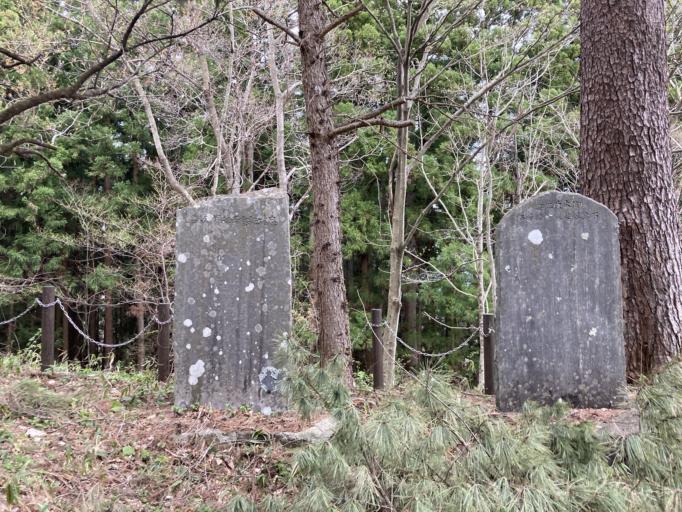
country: JP
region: Iwate
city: Ichinoseki
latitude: 38.9690
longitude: 141.1909
